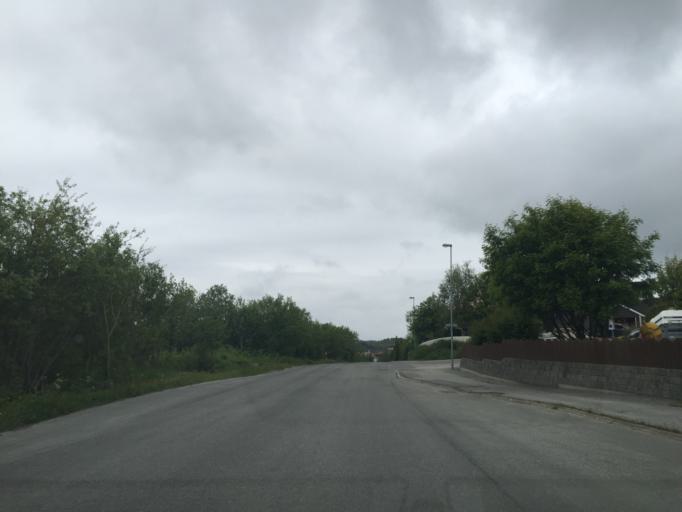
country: NO
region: Nordland
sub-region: Bodo
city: Loding
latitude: 67.2947
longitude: 14.5951
